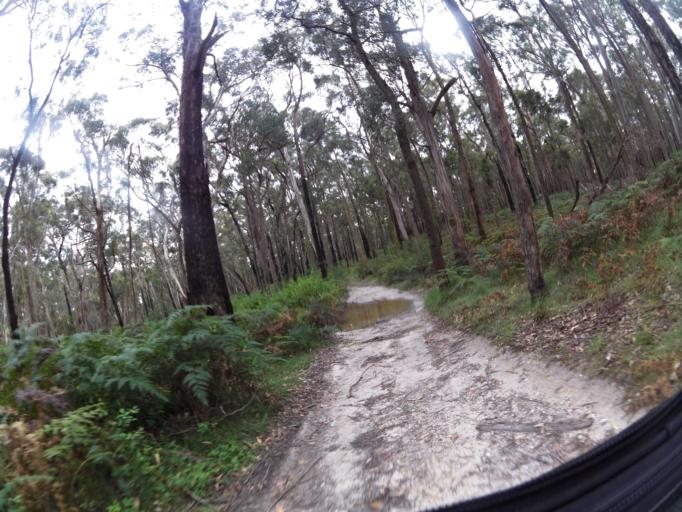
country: AU
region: Victoria
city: Brown Hill
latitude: -37.4924
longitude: 143.9074
